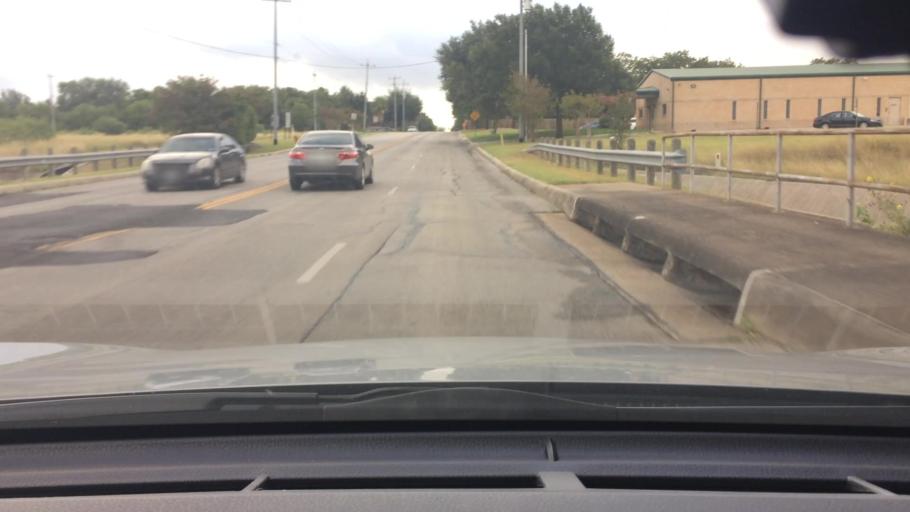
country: US
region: Texas
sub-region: Bexar County
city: Universal City
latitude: 29.5426
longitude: -98.2988
